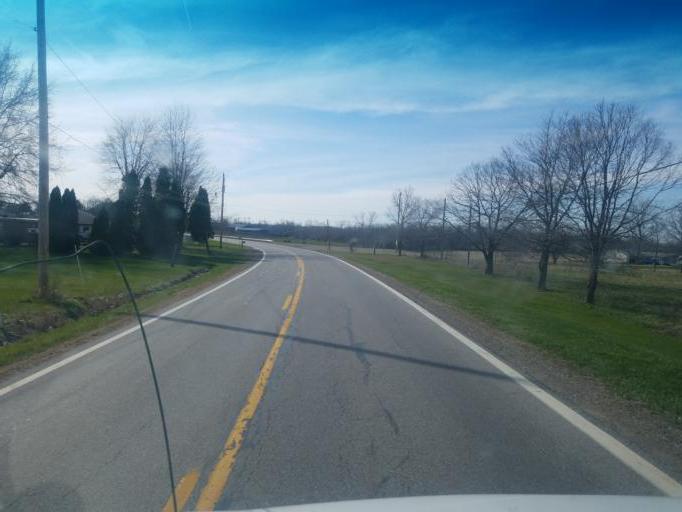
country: US
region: Ohio
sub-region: Champaign County
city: North Lewisburg
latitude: 40.3382
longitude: -83.4716
